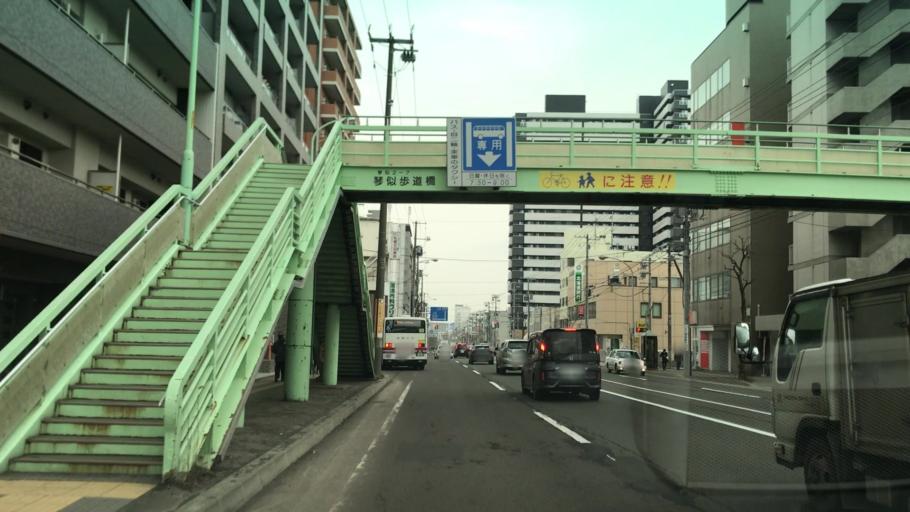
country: JP
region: Hokkaido
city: Sapporo
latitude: 43.0740
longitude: 141.2979
